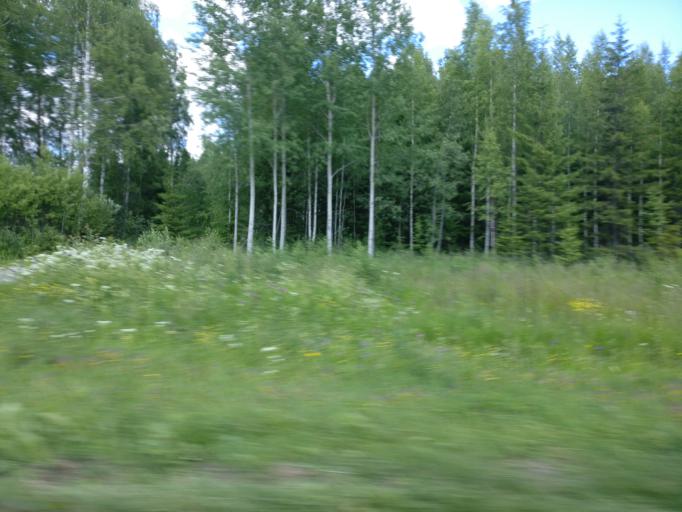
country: FI
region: Southern Savonia
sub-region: Savonlinna
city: Kerimaeki
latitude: 61.8515
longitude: 29.1725
